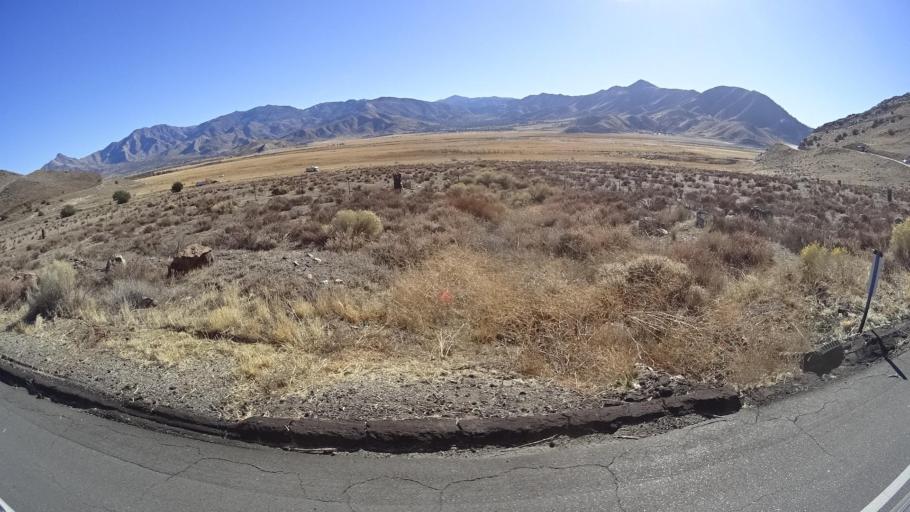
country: US
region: California
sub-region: Kern County
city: Wofford Heights
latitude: 35.6811
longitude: -118.4107
